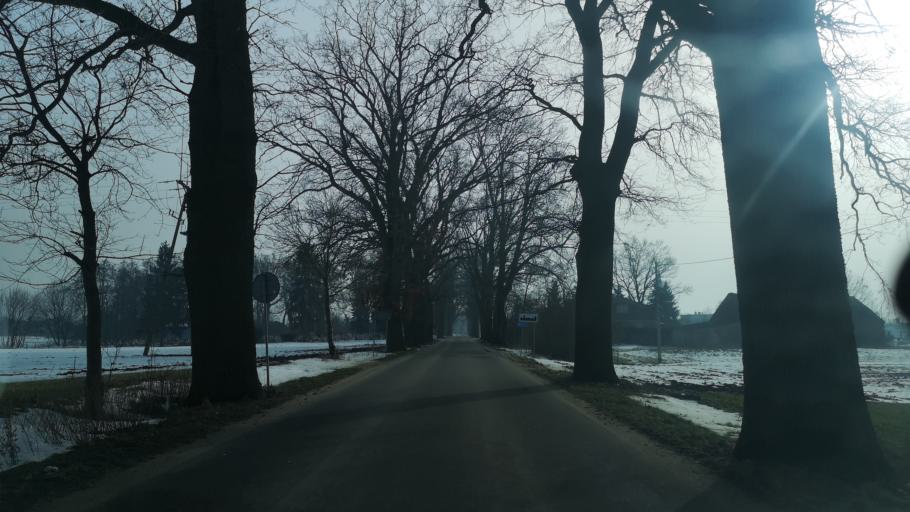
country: PL
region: Warmian-Masurian Voivodeship
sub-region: Powiat nowomiejski
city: Biskupiec
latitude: 53.5065
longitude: 19.3512
